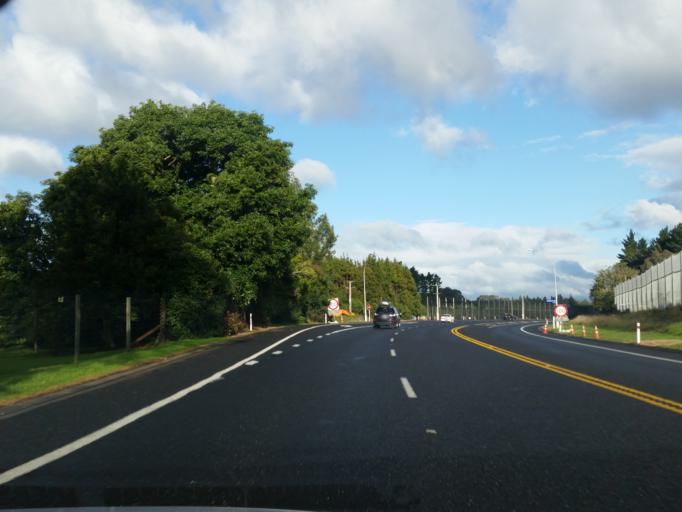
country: NZ
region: Bay of Plenty
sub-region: Western Bay of Plenty District
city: Katikati
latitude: -37.6158
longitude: 175.9500
